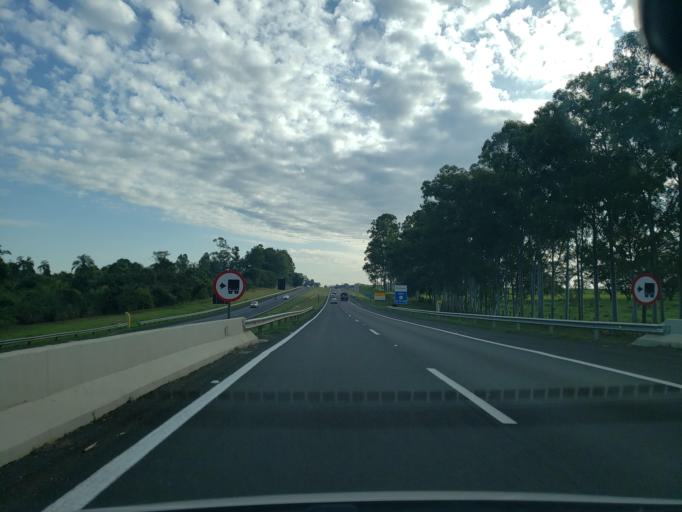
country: BR
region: Sao Paulo
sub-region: Guararapes
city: Guararapes
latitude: -21.2076
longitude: -50.6512
